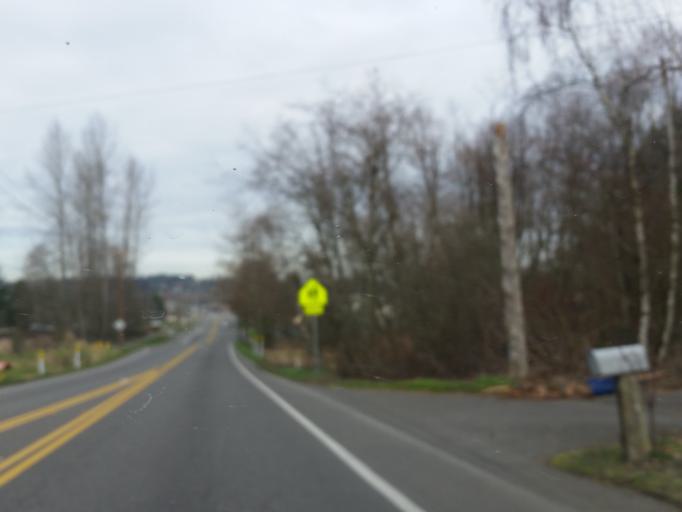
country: US
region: Washington
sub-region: Pierce County
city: Sumner
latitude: 47.1799
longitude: -122.2561
